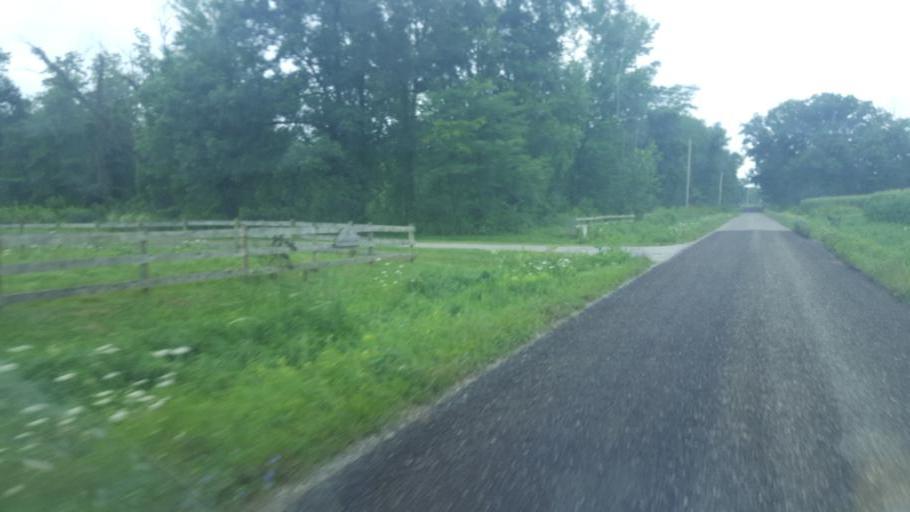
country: US
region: Ohio
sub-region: Knox County
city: Centerburg
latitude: 40.3801
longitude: -82.7501
